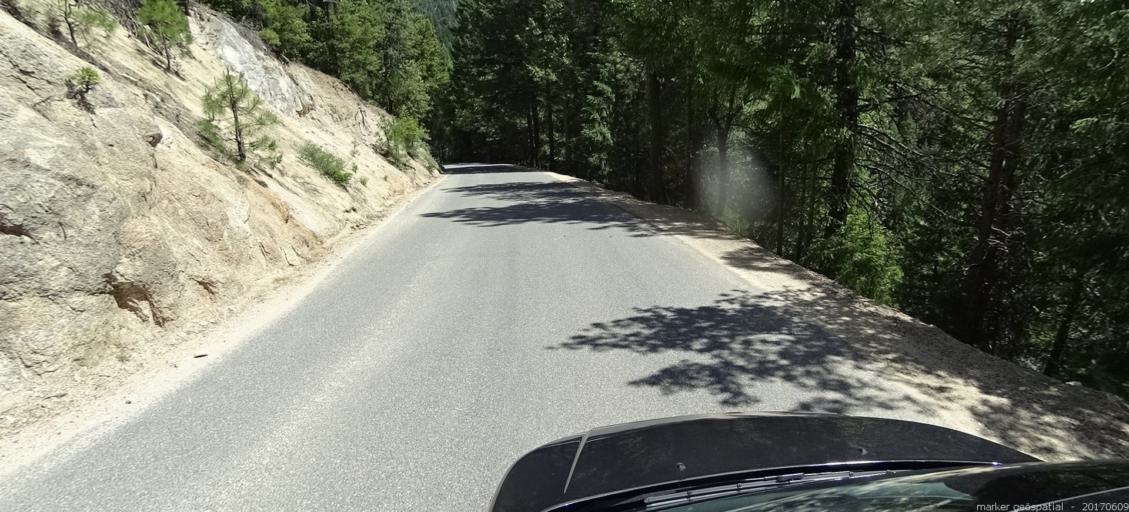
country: US
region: California
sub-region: Siskiyou County
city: Yreka
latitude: 41.4264
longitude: -122.9308
